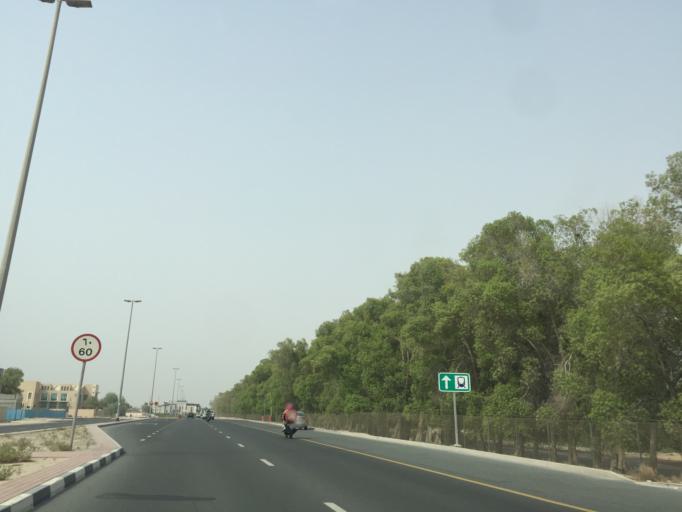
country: AE
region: Dubai
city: Dubai
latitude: 25.1263
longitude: 55.1877
